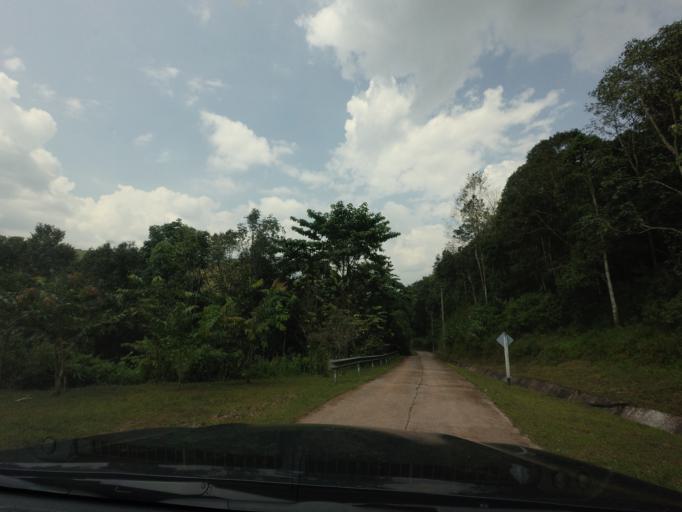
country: TH
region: Nan
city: Bo Kluea
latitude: 19.1811
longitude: 101.1779
